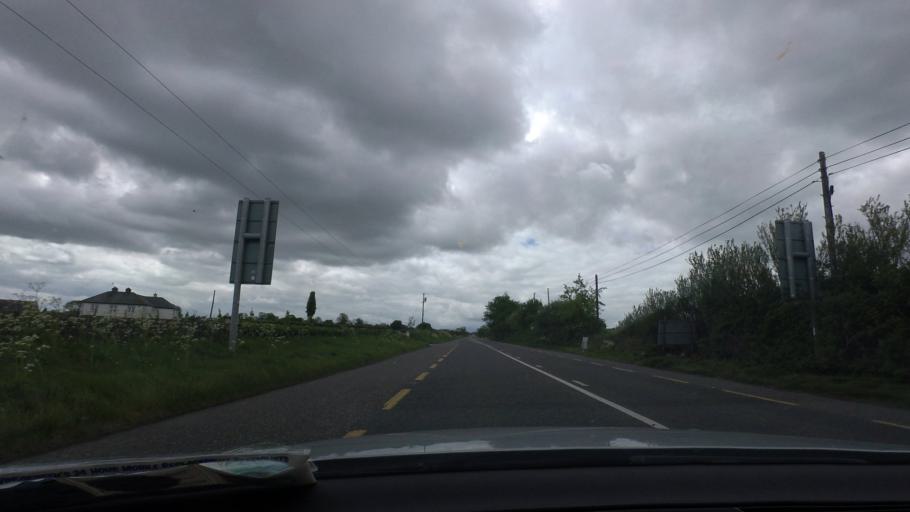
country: IE
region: Munster
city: Thurles
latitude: 52.6118
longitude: -7.7814
